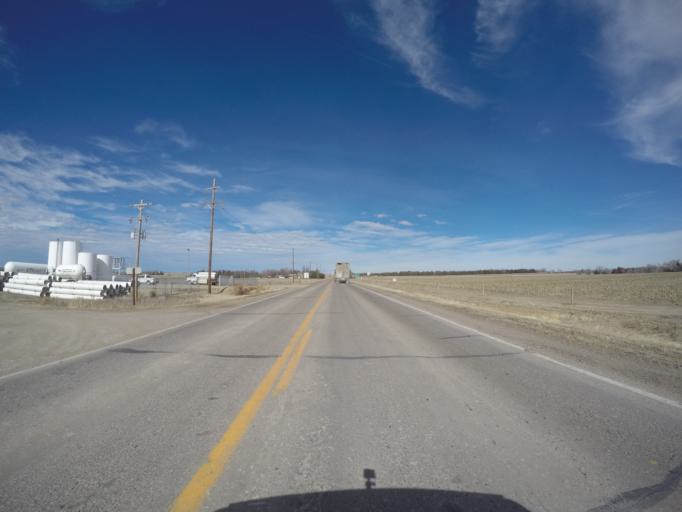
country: US
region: Nebraska
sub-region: Franklin County
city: Franklin
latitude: 40.1041
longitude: -98.9523
